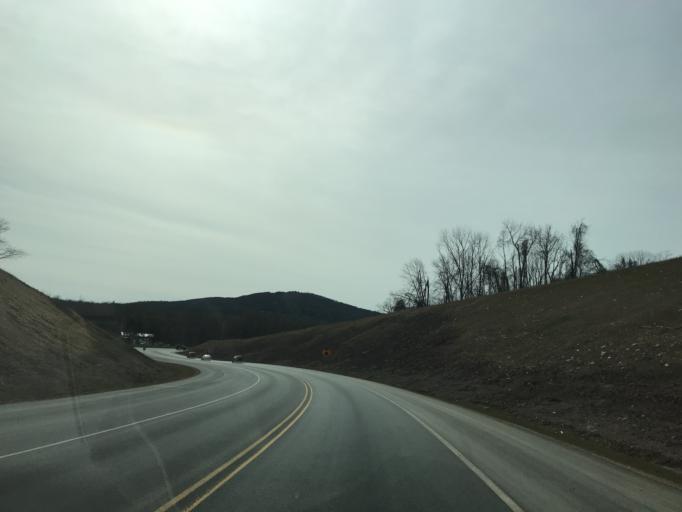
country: US
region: Pennsylvania
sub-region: Northumberland County
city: Northumberland
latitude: 40.9185
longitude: -76.8397
